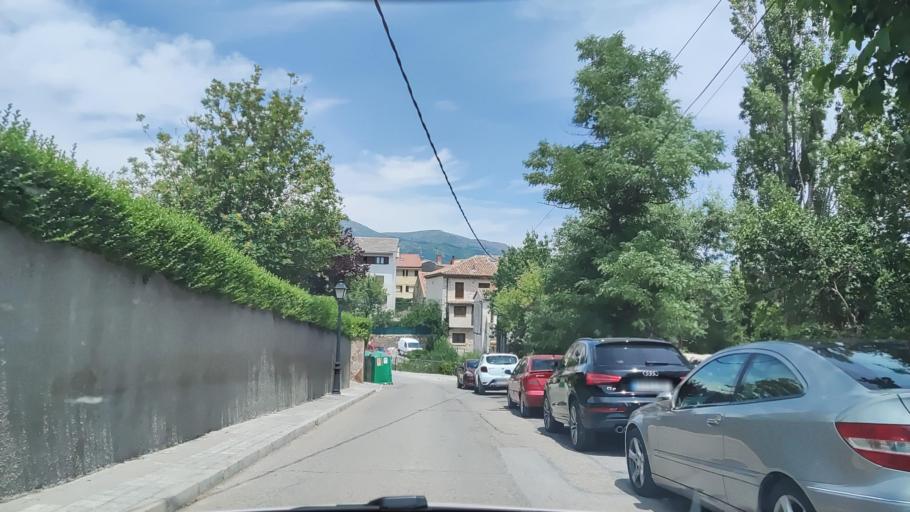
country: ES
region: Madrid
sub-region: Provincia de Madrid
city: Rascafria
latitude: 40.9037
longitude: -3.8814
